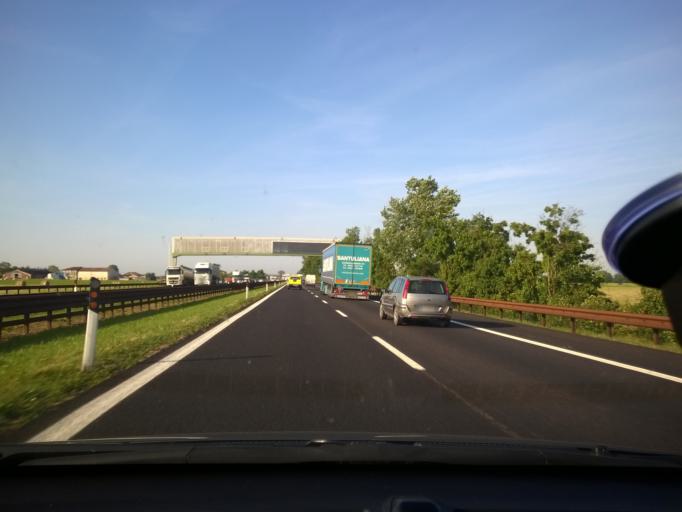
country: IT
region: Lombardy
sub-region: Provincia di Mantova
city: Bondeno
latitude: 44.9296
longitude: 10.8582
